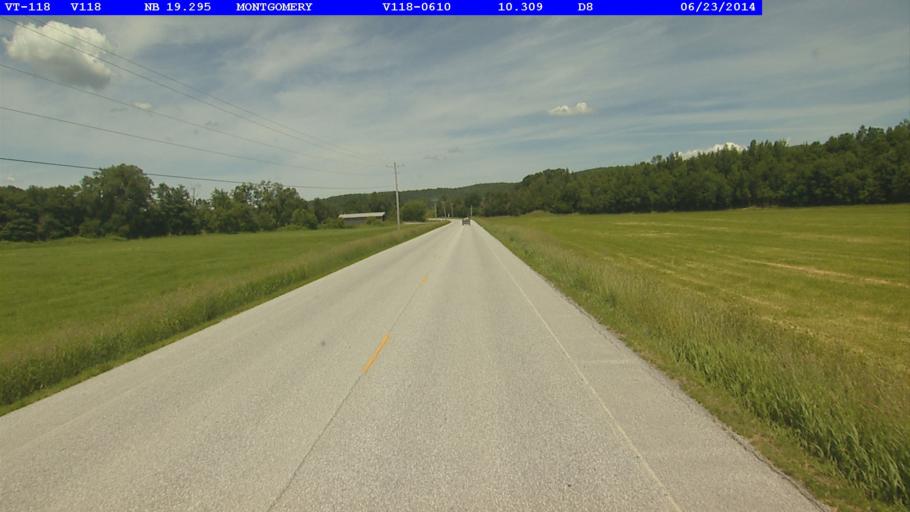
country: US
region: Vermont
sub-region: Franklin County
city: Richford
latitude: 44.9183
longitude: -72.6706
